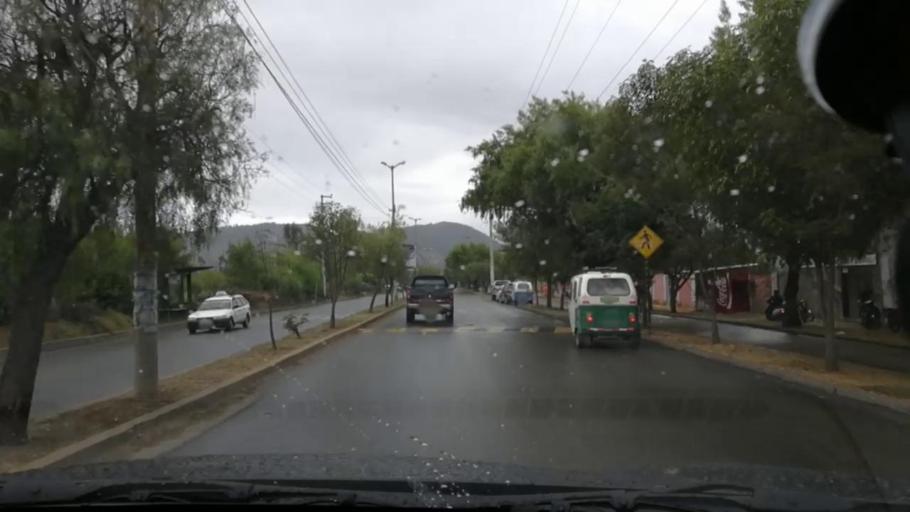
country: PE
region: Cajamarca
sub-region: Provincia de Cajamarca
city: Cajamarca
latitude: -7.1653
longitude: -78.4899
